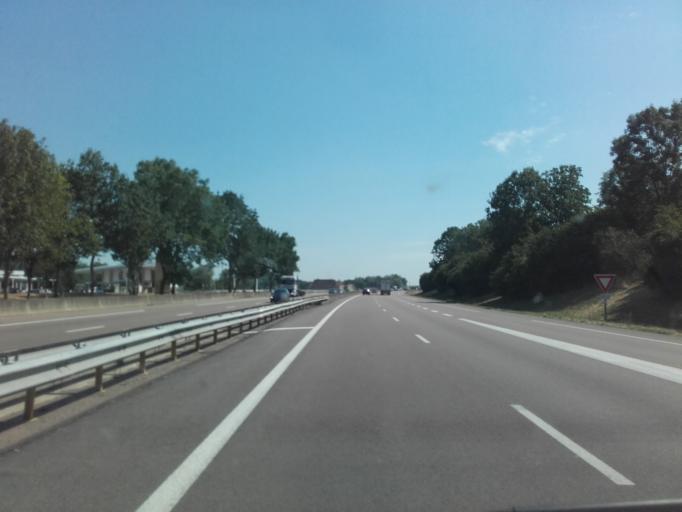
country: FR
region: Bourgogne
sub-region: Departement de la Cote-d'Or
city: Pouilly-en-Auxois
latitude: 47.3106
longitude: 4.5001
